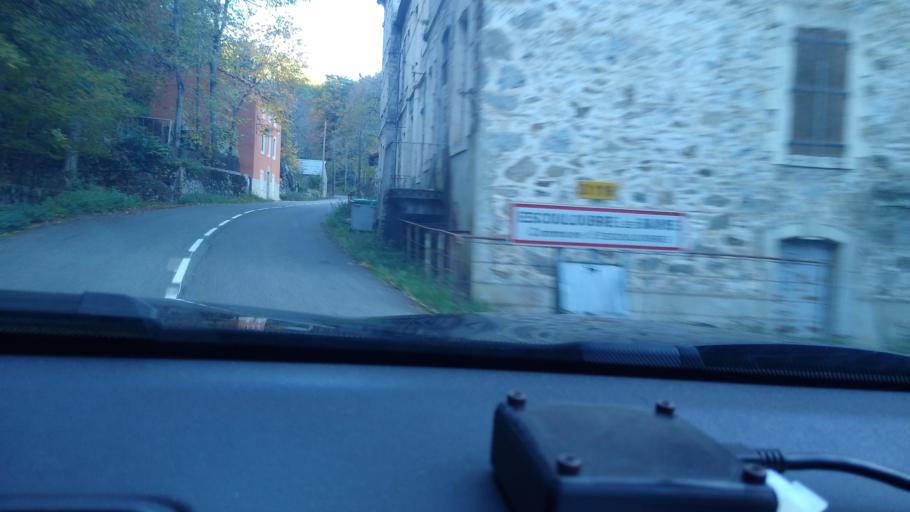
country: FR
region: Languedoc-Roussillon
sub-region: Departement de l'Aude
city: Quillan
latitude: 42.7248
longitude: 2.1151
